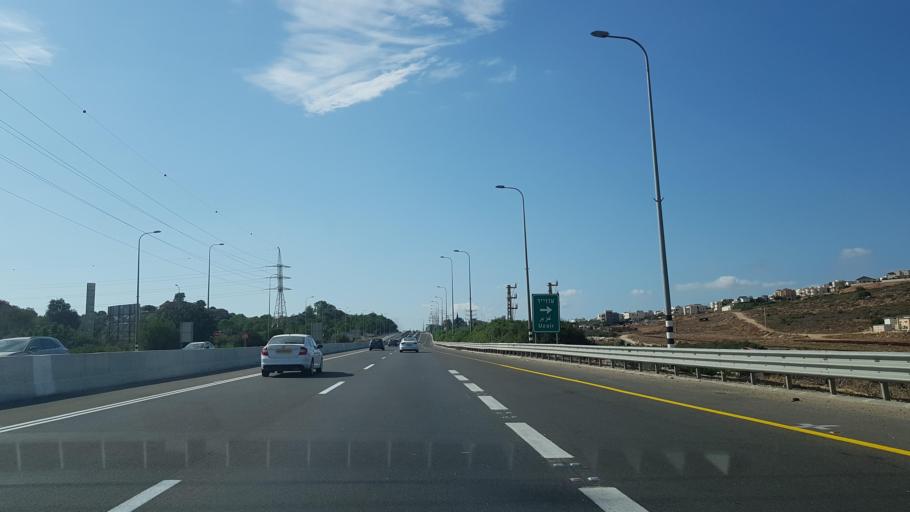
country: IL
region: Northern District
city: Rumat Heib
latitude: 32.7661
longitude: 35.3163
